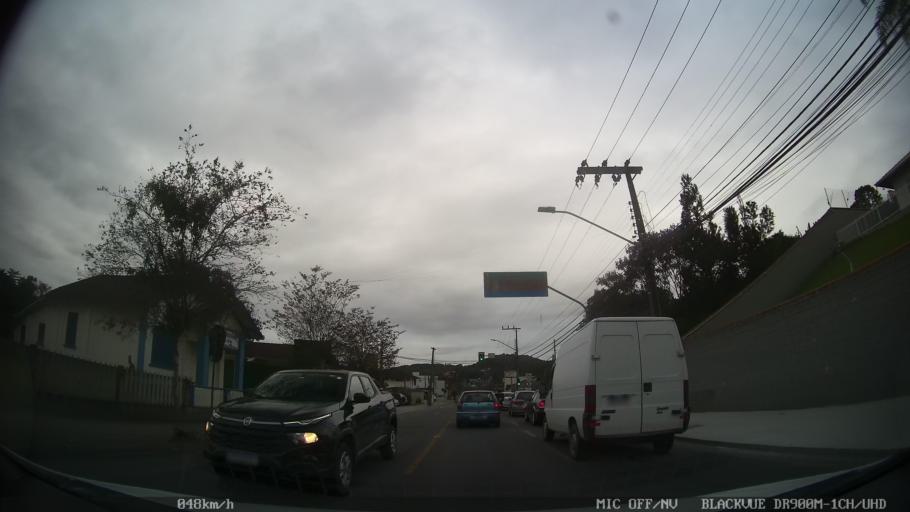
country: BR
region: Santa Catarina
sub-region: Joinville
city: Joinville
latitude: -26.2916
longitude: -48.8680
